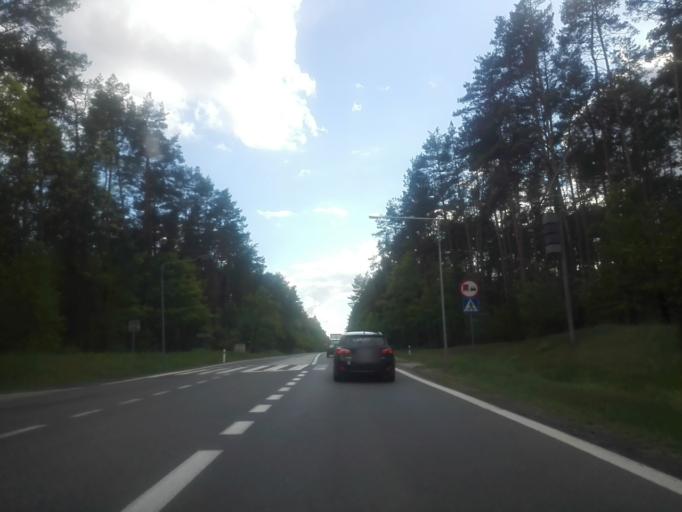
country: PL
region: Masovian Voivodeship
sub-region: Powiat wyszkowski
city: Dlugosiodlo
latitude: 52.7046
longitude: 21.6759
